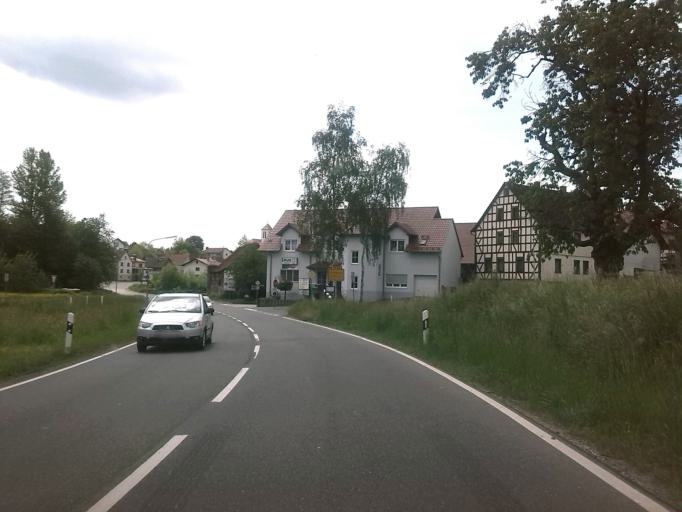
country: DE
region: Hesse
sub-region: Regierungsbezirk Darmstadt
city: Furth
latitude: 49.6677
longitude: 8.8009
